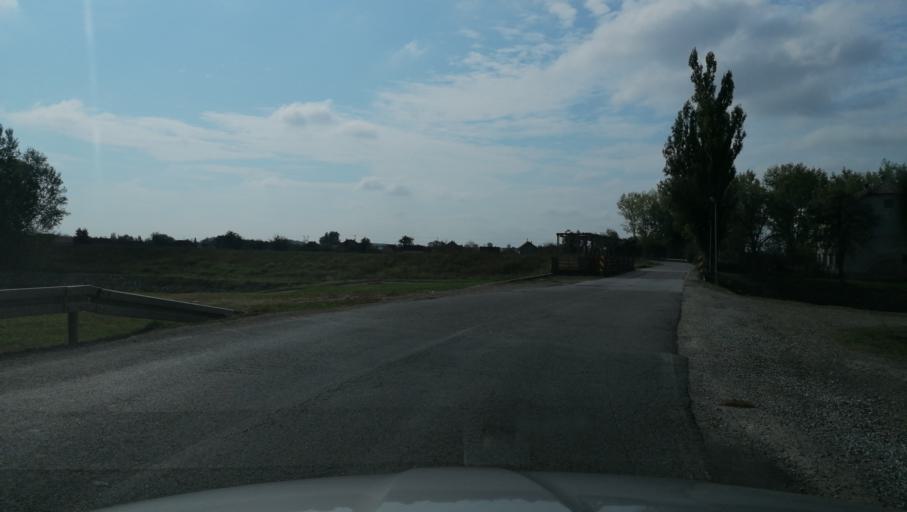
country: RS
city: Bosut
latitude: 44.9432
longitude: 19.3682
